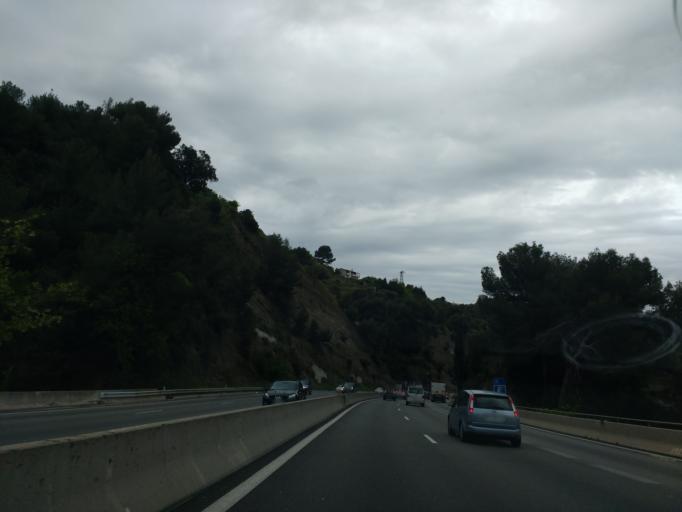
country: FR
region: Provence-Alpes-Cote d'Azur
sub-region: Departement des Alpes-Maritimes
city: Colomars
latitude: 43.7143
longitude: 7.2136
